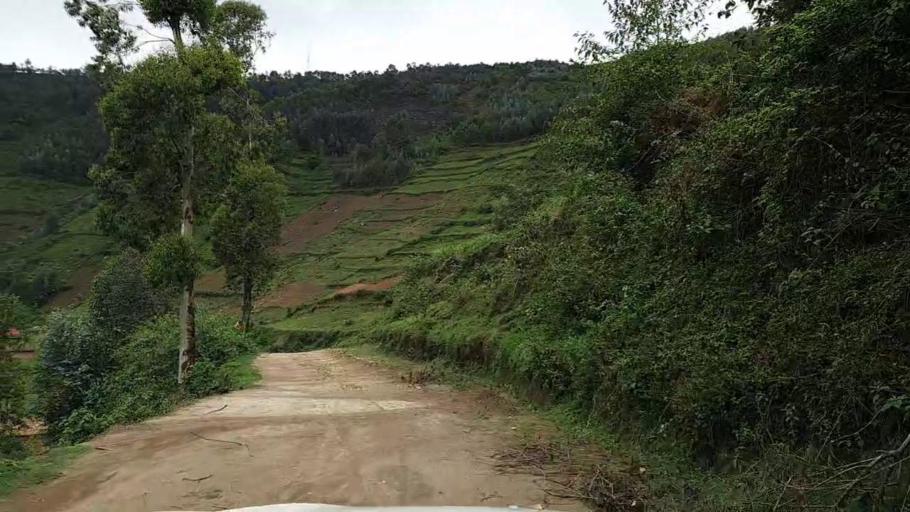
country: RW
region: Southern Province
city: Gikongoro
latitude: -2.3611
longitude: 29.4969
